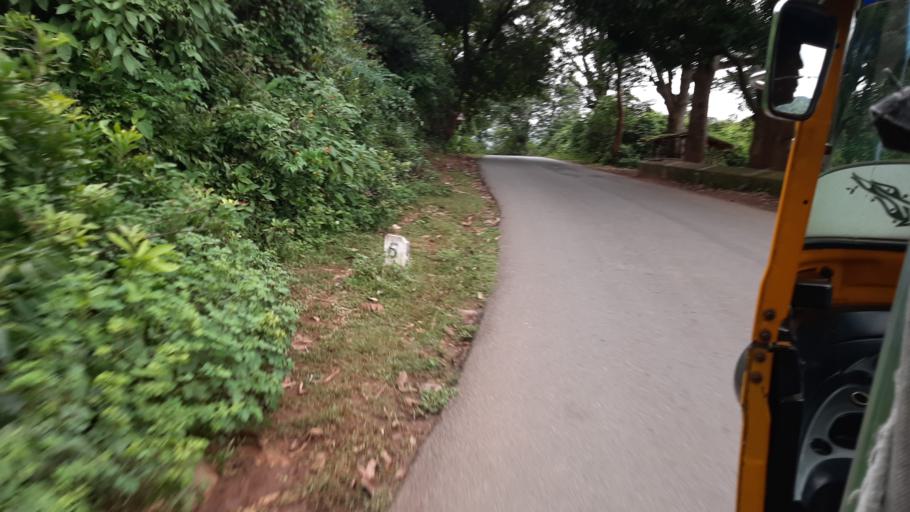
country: IN
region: Andhra Pradesh
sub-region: Vizianagaram District
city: Salur
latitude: 18.2457
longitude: 83.0250
